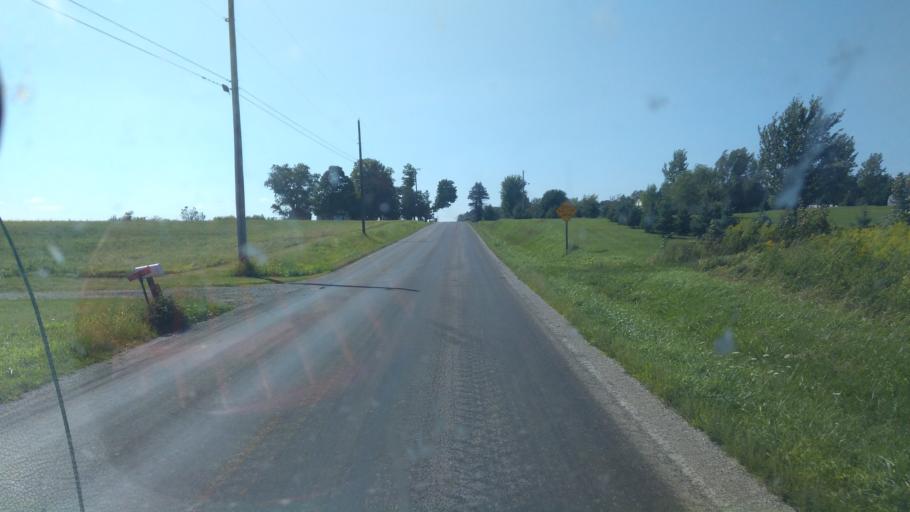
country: US
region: Ohio
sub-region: Ashland County
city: Ashland
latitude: 40.9695
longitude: -82.3016
